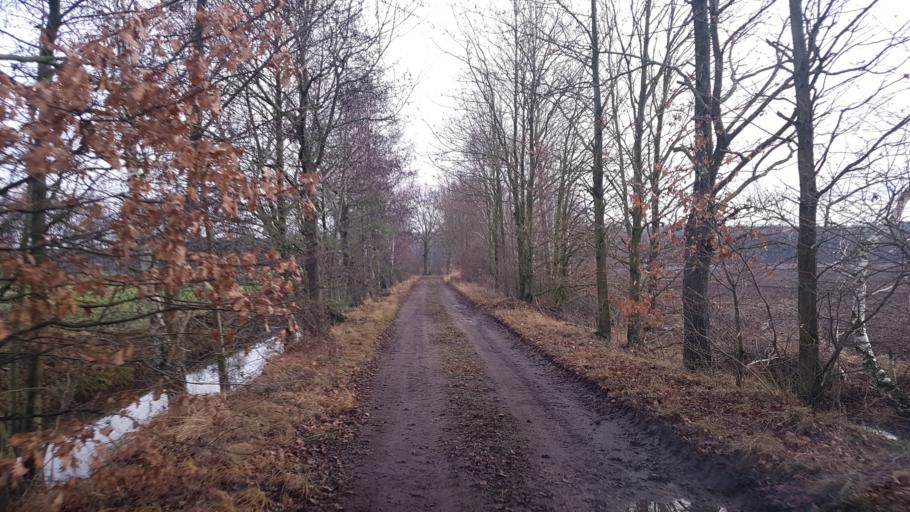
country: DE
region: Brandenburg
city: Ruckersdorf
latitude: 51.5901
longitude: 13.6179
